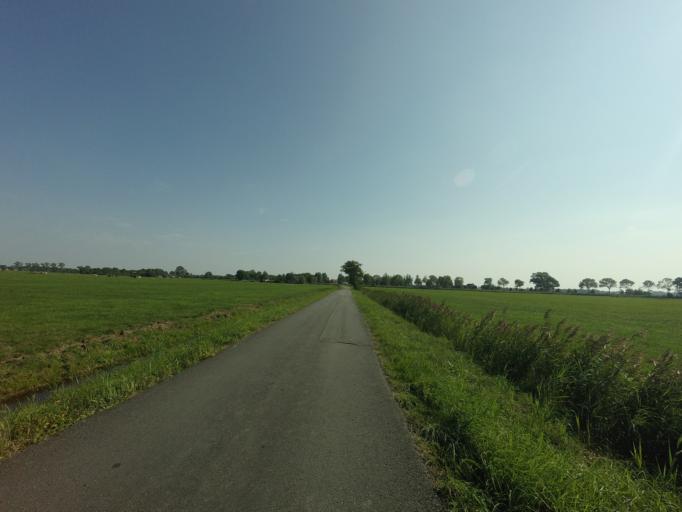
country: NL
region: Groningen
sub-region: Gemeente Zuidhorn
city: Zuidhorn
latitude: 53.2135
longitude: 6.4329
